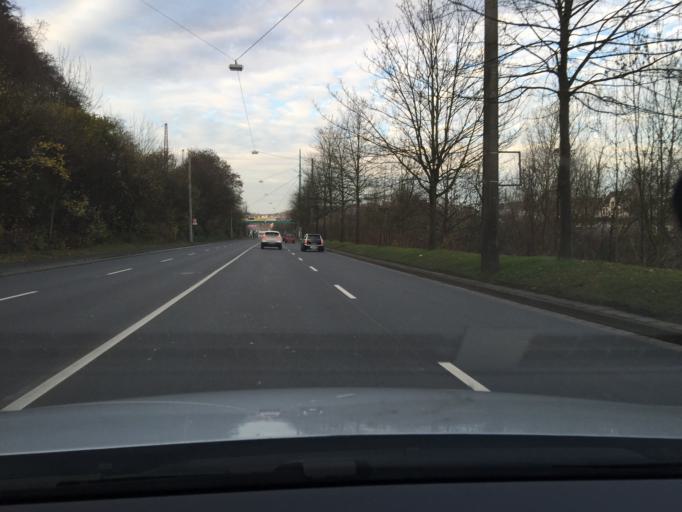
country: DE
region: North Rhine-Westphalia
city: Herdecke
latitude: 51.3794
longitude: 7.4507
